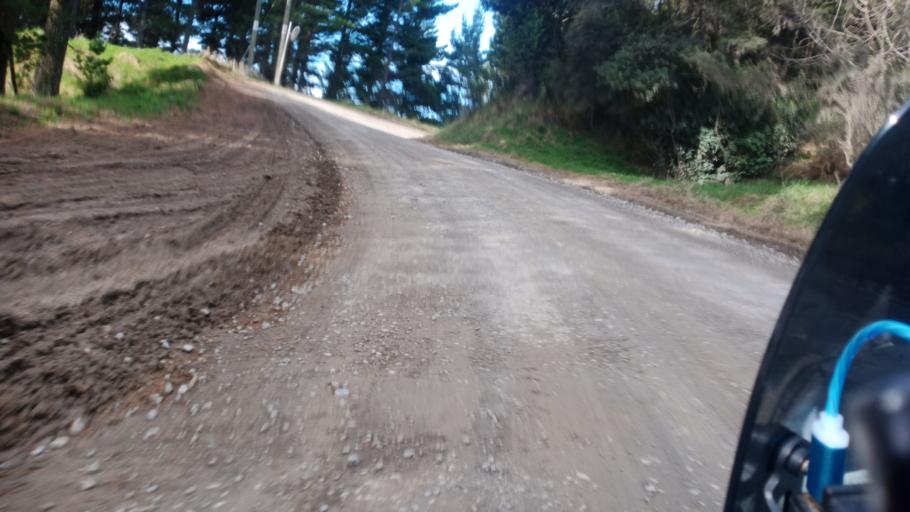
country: NZ
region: Gisborne
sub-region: Gisborne District
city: Gisborne
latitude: -38.1269
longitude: 178.1664
